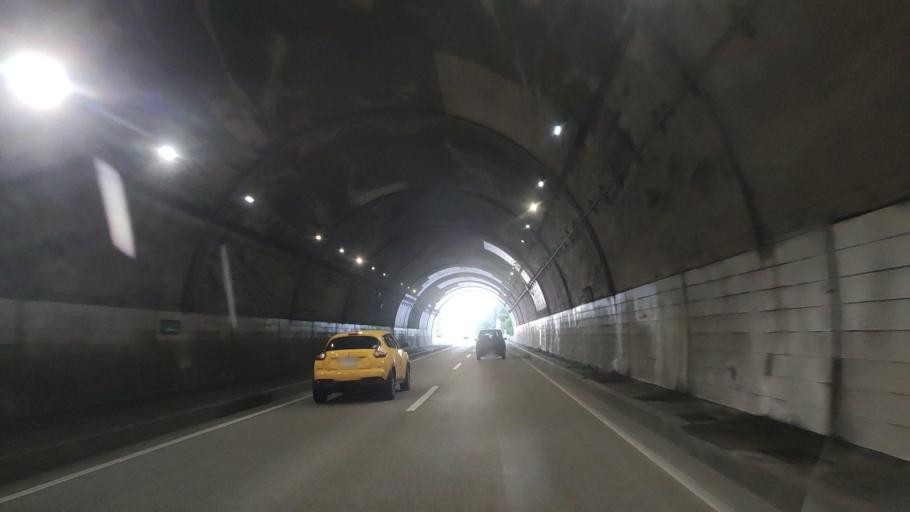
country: JP
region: Toyama
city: Himi
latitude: 36.8530
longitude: 136.9775
